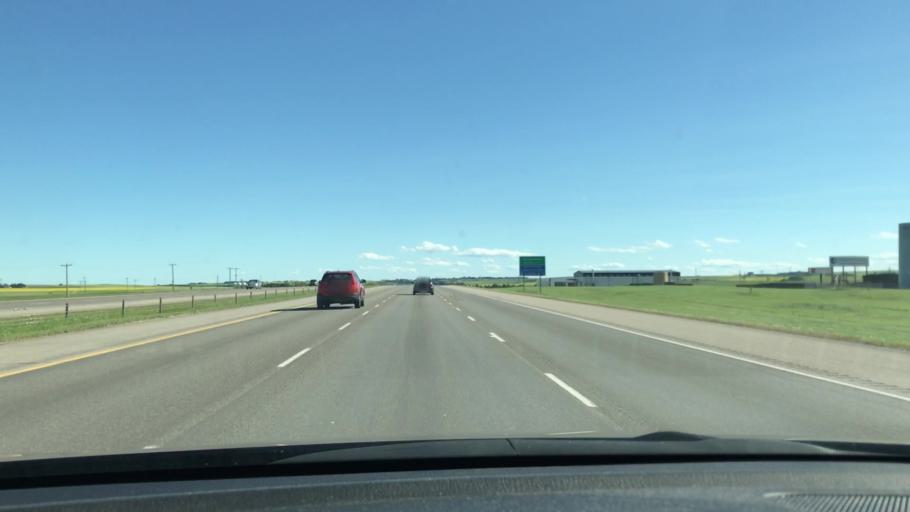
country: CA
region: Alberta
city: Crossfield
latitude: 51.4972
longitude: -114.0254
